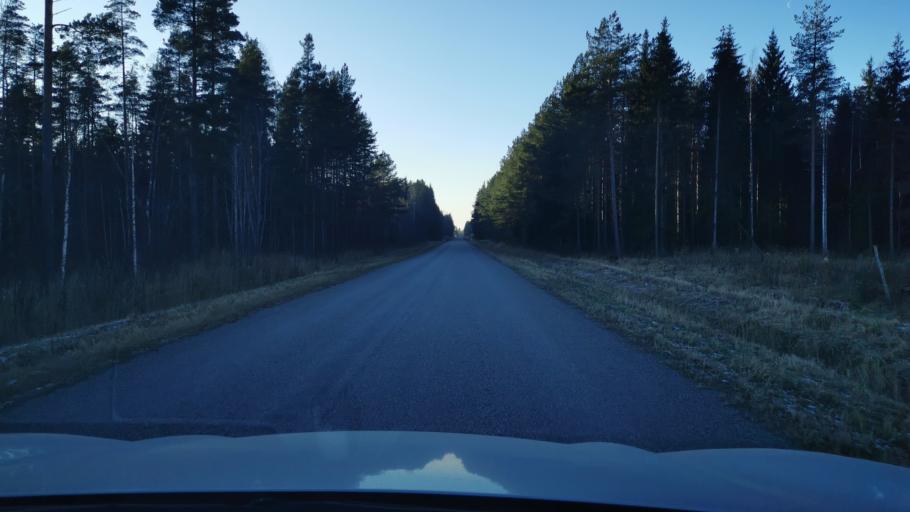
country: EE
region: Ida-Virumaa
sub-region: Kivioli linn
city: Kivioli
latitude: 59.2239
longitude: 26.9578
